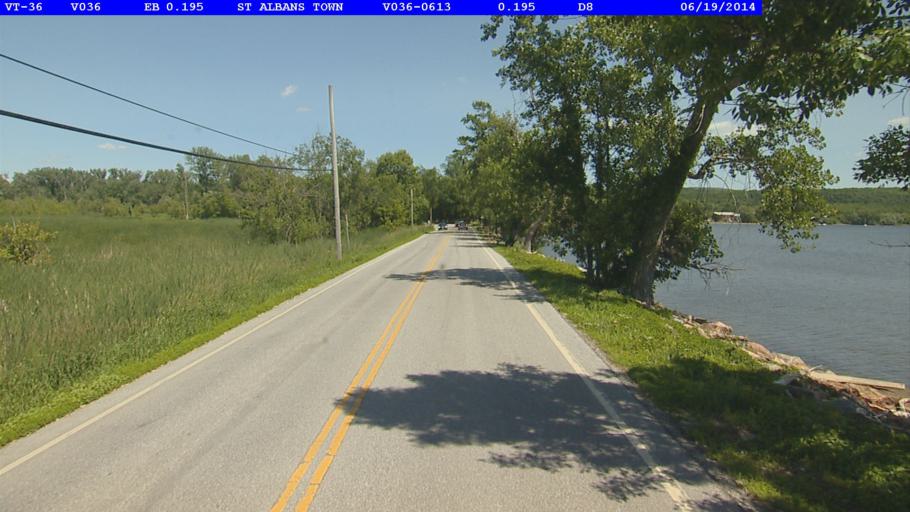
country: US
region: Vermont
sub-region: Franklin County
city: Saint Albans
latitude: 44.8103
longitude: -73.1476
